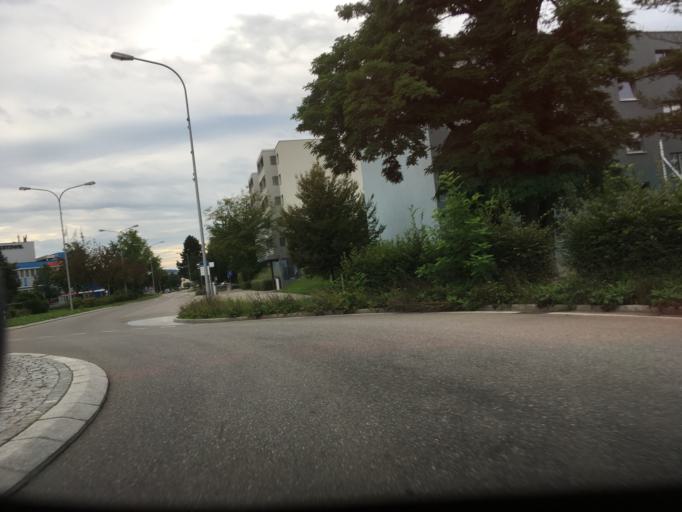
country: CH
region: Zurich
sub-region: Bezirk Uster
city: Hegnau / Sunnebueel-Eich
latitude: 47.3893
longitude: 8.6826
